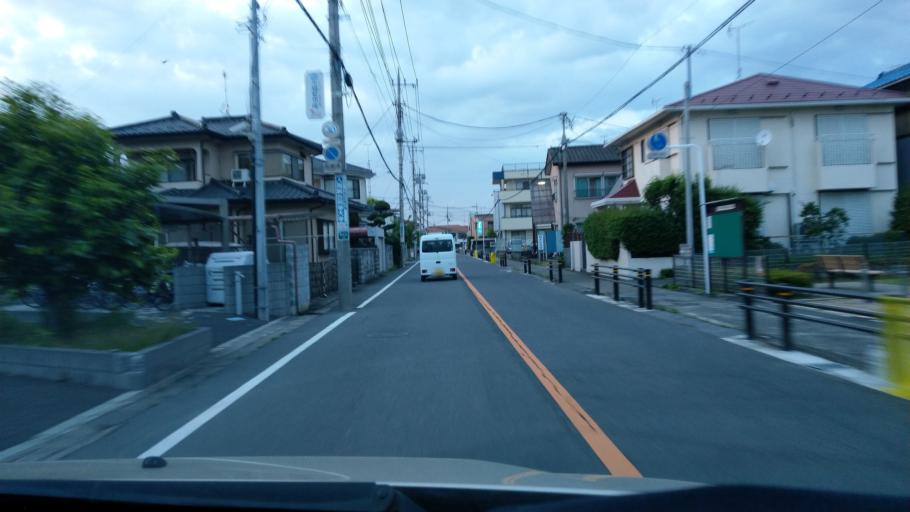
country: JP
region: Saitama
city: Iwatsuki
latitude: 35.9551
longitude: 139.6966
